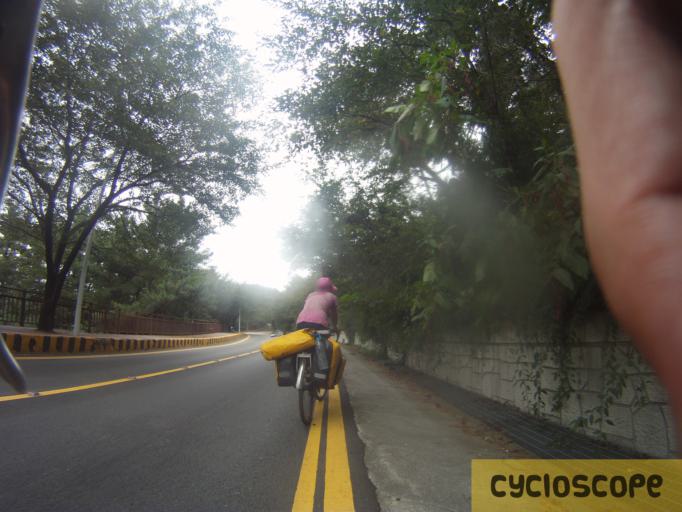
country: KR
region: Busan
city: Kijang
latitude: 35.1723
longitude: 129.1944
